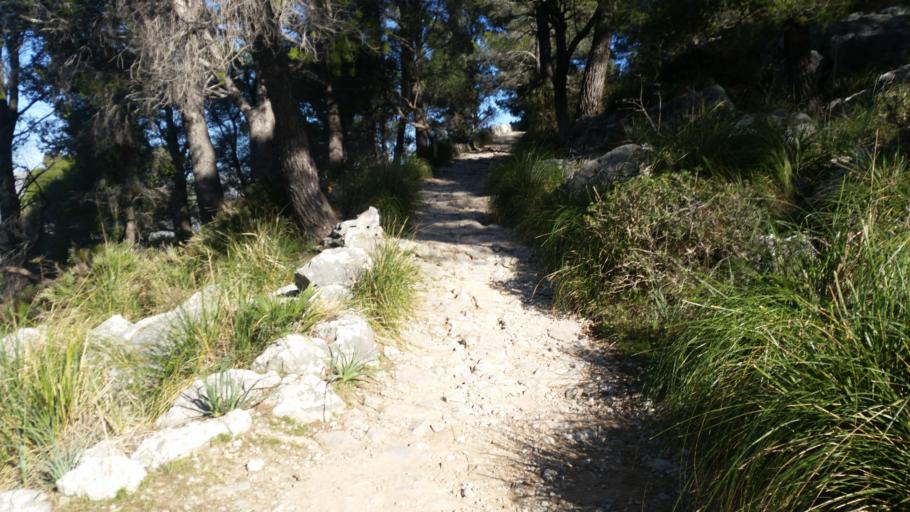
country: ES
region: Balearic Islands
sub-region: Illes Balears
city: Pollenca
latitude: 39.8684
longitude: 3.0210
